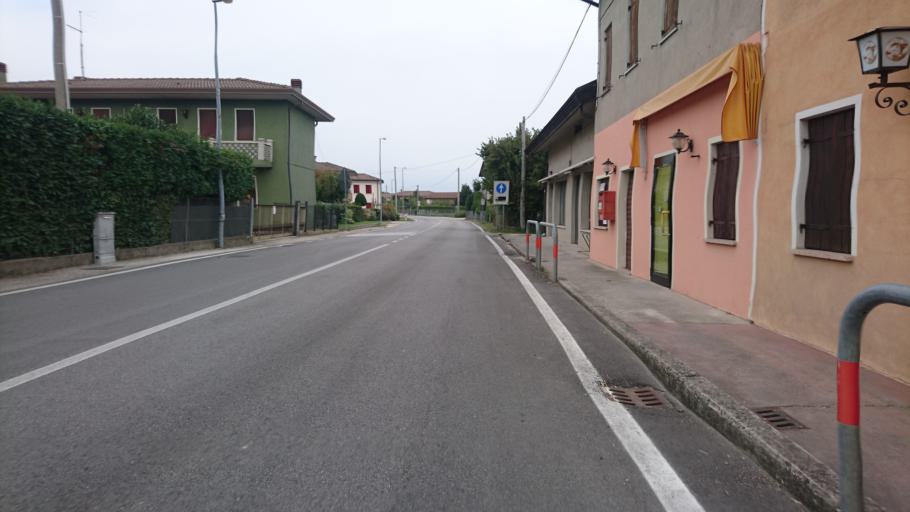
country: IT
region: Veneto
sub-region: Provincia di Padova
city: Curtarolo
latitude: 45.5336
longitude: 11.8394
